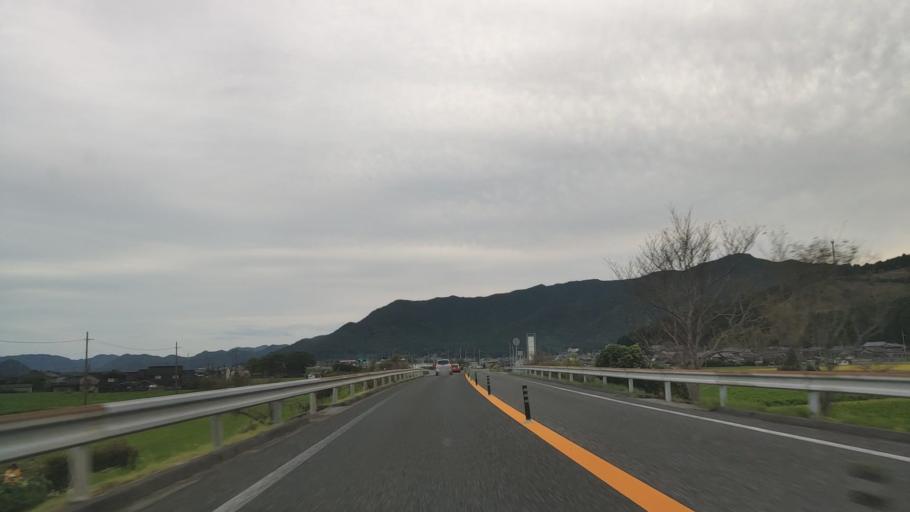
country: JP
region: Hyogo
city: Nishiwaki
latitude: 35.0617
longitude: 134.7696
